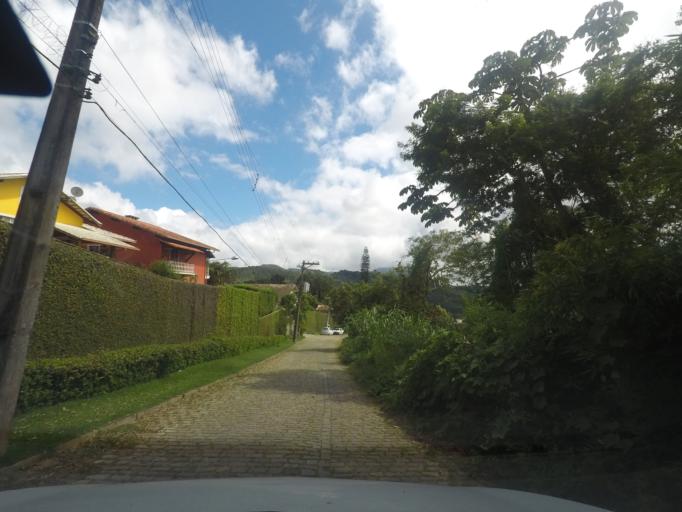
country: BR
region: Rio de Janeiro
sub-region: Teresopolis
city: Teresopolis
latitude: -22.3966
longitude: -42.9888
